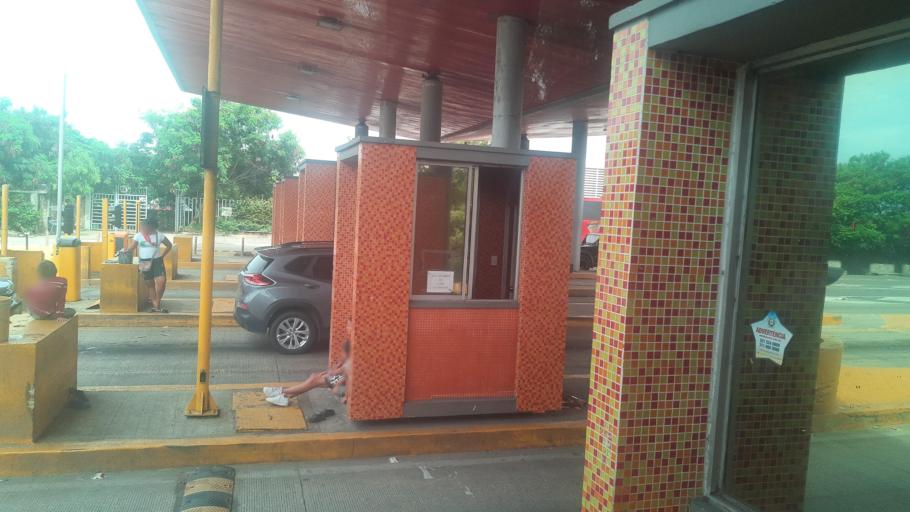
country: CO
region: Atlantico
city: Barranquilla
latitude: 10.9789
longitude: -74.7296
